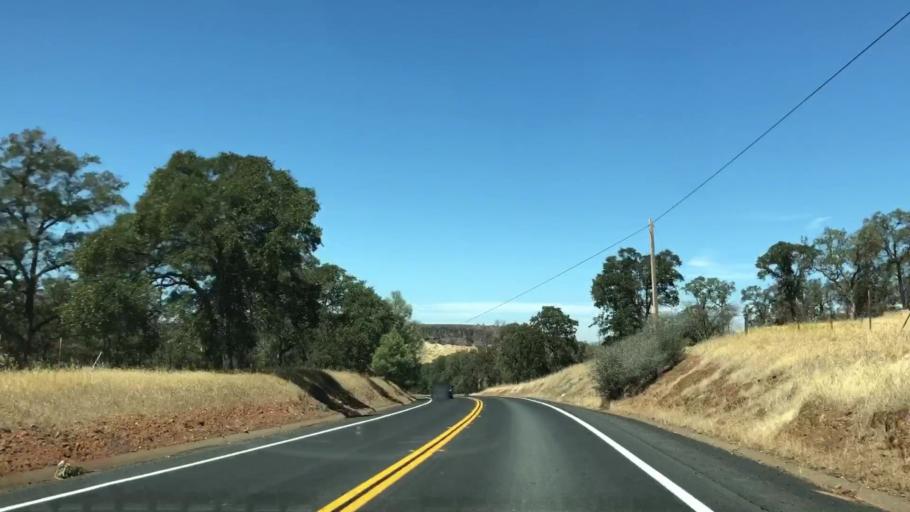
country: US
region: California
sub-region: Calaveras County
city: Copperopolis
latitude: 37.8971
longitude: -120.5552
